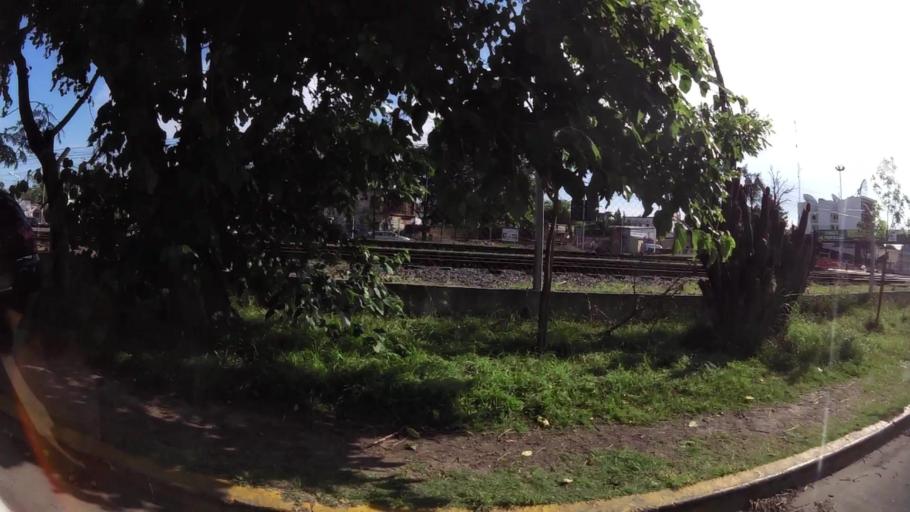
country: AR
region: Buenos Aires
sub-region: Partido de Merlo
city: Merlo
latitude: -34.6653
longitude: -58.7217
